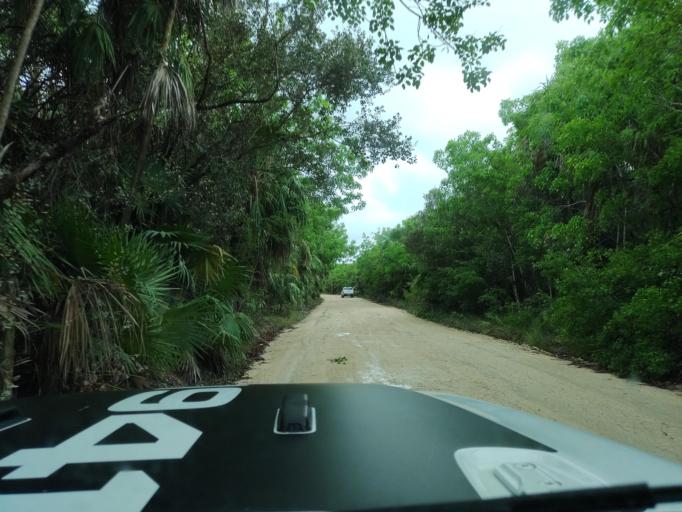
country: MX
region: Quintana Roo
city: Tulum
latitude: 20.0641
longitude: -87.4800
